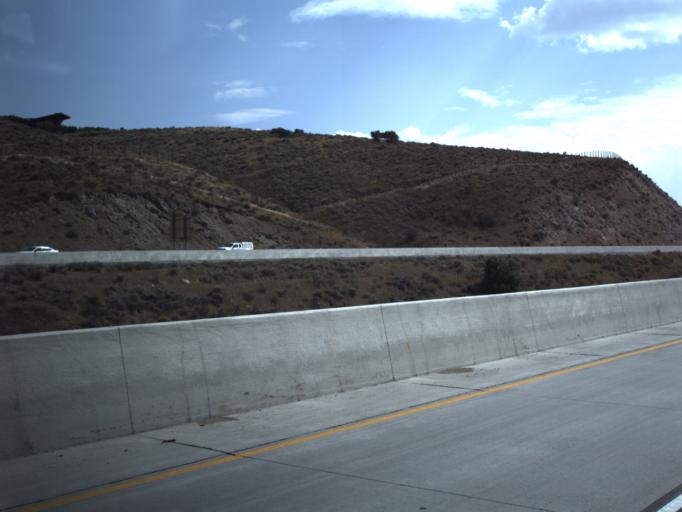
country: US
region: Utah
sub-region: Summit County
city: Snyderville
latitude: 40.7602
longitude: -111.4718
